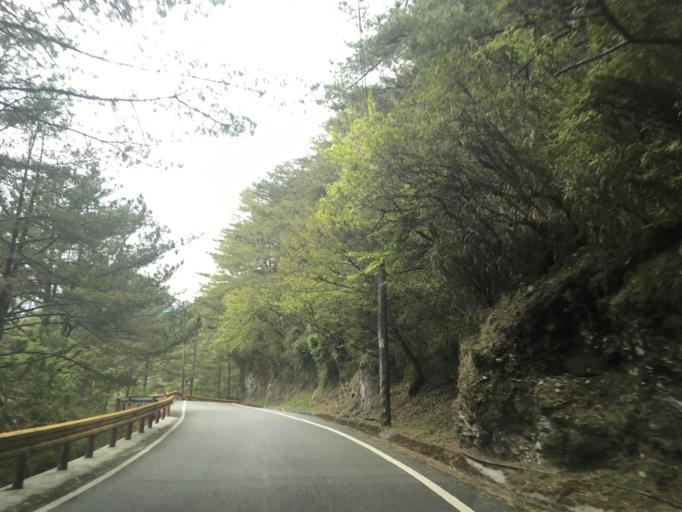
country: TW
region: Taiwan
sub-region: Hualien
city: Hualian
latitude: 24.1809
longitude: 121.3213
